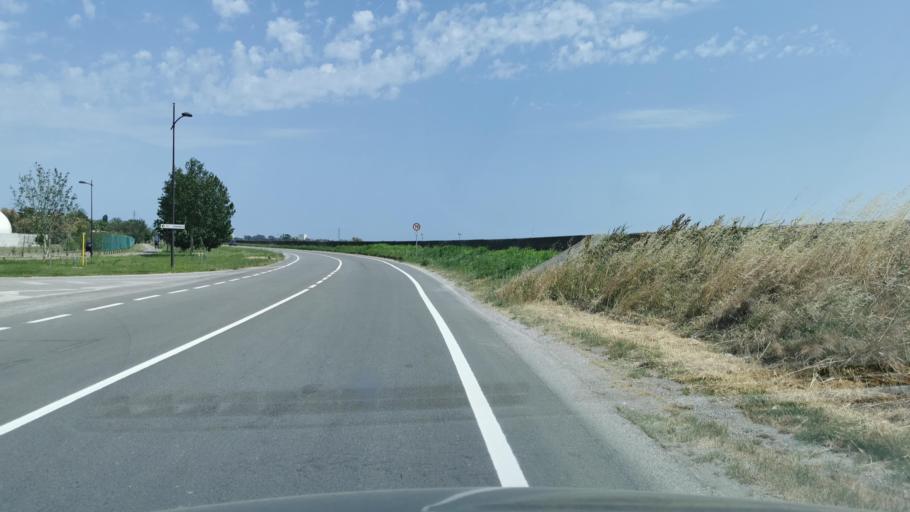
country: IT
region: Emilia-Romagna
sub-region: Provincia di Ferrara
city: Comacchio
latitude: 44.6782
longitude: 12.2037
